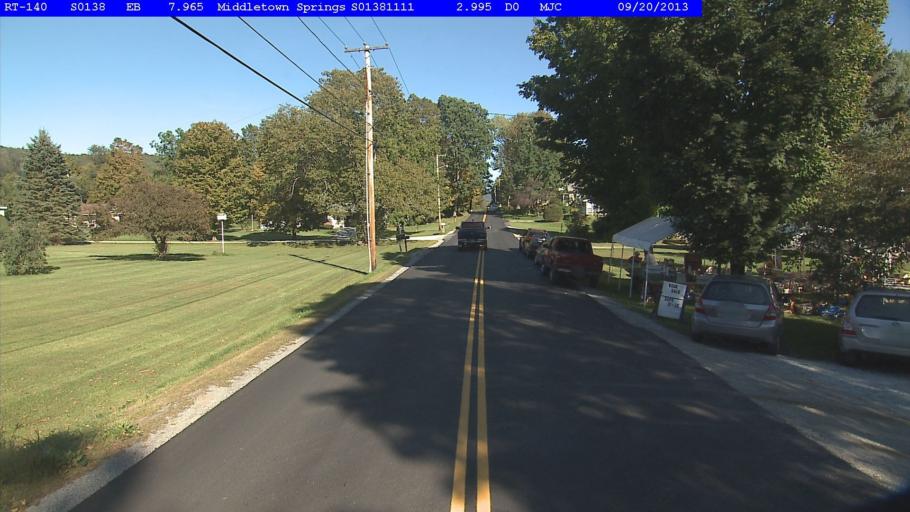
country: US
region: Vermont
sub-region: Rutland County
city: Poultney
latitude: 43.4853
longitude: -73.1224
